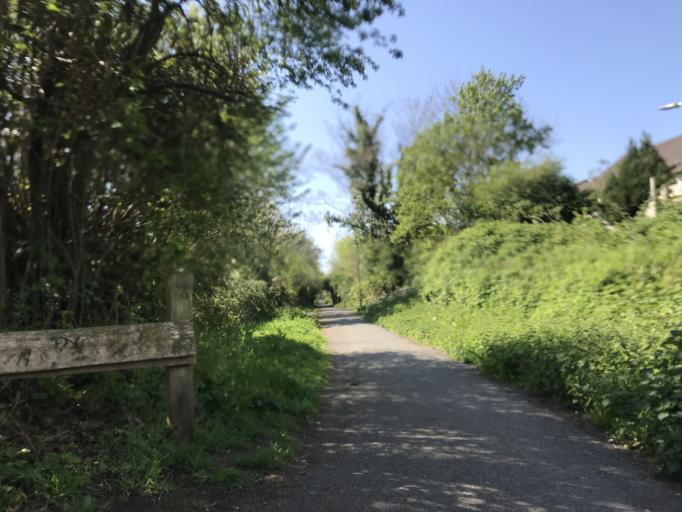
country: GB
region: England
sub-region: Devon
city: Barnstaple
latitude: 51.0717
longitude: -4.0431
